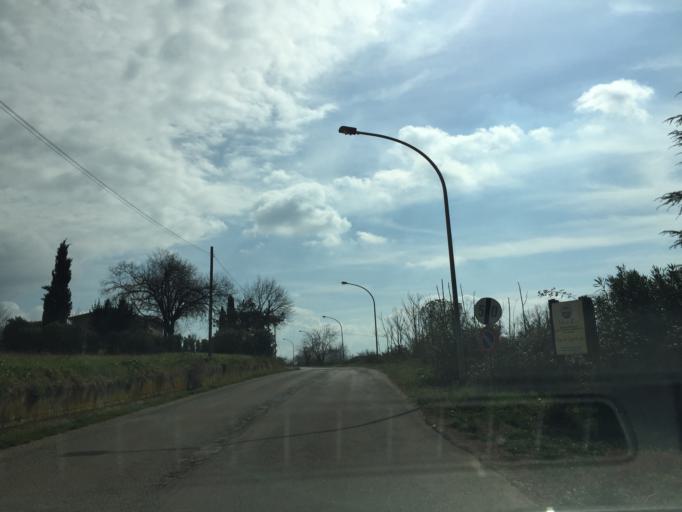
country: IT
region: Latium
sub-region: Provincia di Frosinone
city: Castrocielo
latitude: 41.5187
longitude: 13.7091
